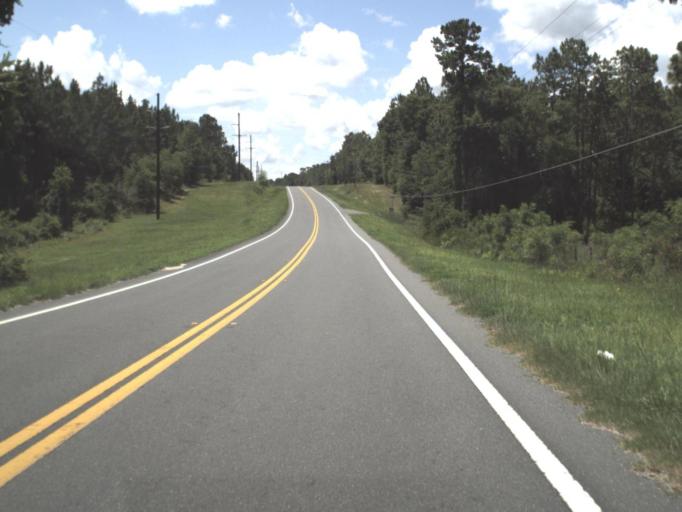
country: US
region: Florida
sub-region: Alachua County
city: Hawthorne
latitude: 29.6433
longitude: -82.0328
